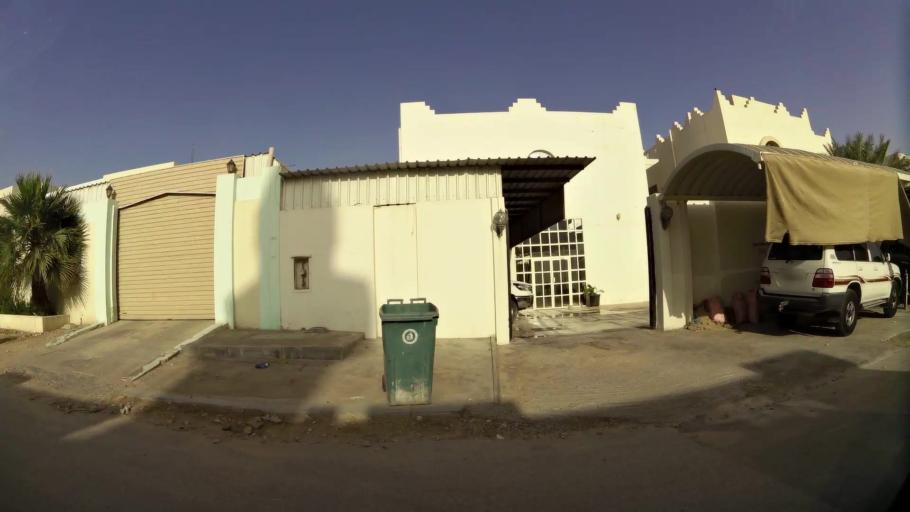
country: QA
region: Baladiyat ar Rayyan
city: Ar Rayyan
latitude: 25.3401
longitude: 51.4361
